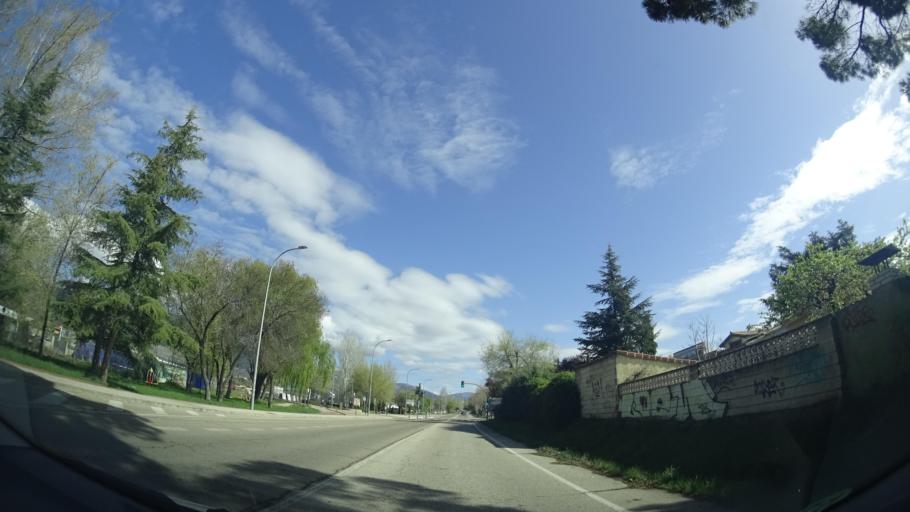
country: ES
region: Madrid
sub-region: Provincia de Madrid
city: Miraflores de la Sierra
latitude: 40.7460
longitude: -3.7841
